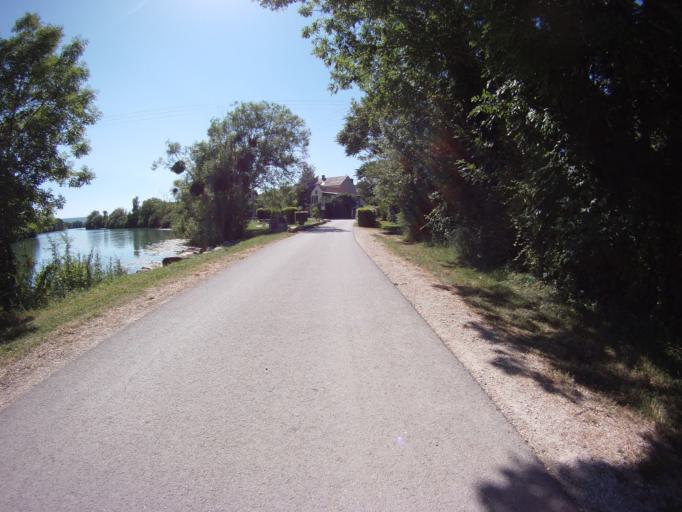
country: FR
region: Champagne-Ardenne
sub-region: Departement de la Marne
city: Dormans
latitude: 49.0910
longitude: 3.6470
